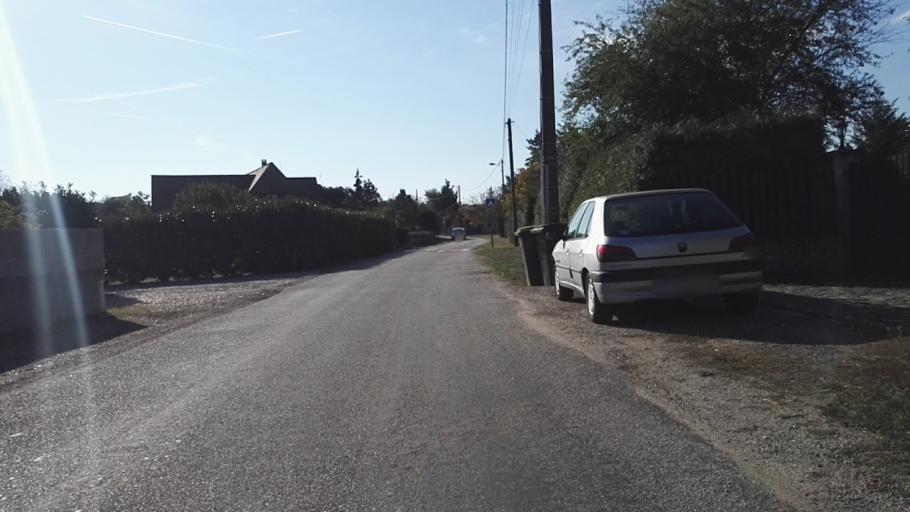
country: FR
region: Haute-Normandie
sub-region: Departement de l'Eure
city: Menilles
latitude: 49.0442
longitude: 1.3382
